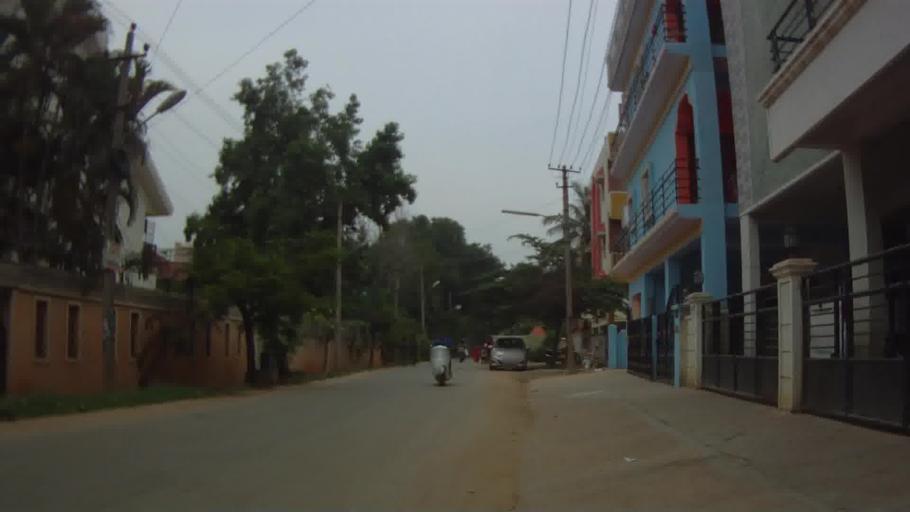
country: IN
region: Karnataka
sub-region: Bangalore Urban
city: Bangalore
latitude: 12.9579
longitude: 77.7219
